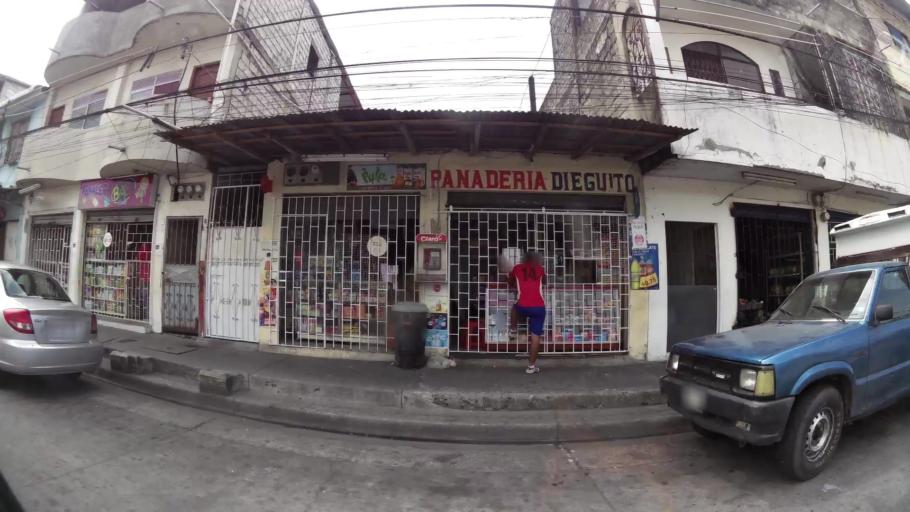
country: EC
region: Guayas
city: Guayaquil
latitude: -2.2321
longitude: -79.9056
